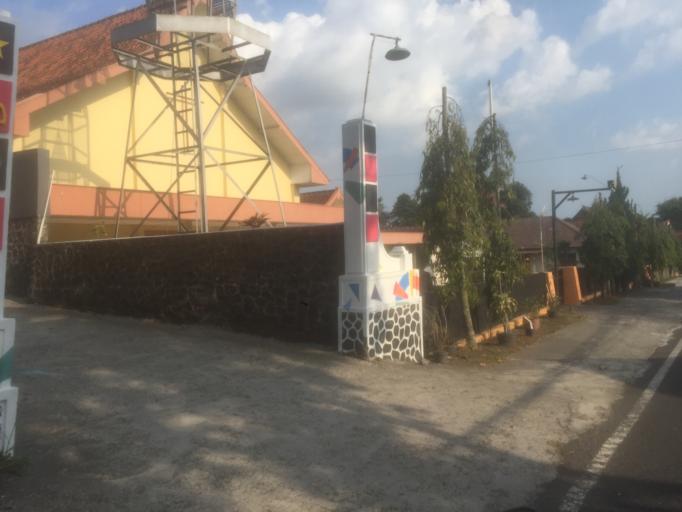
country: ID
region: Daerah Istimewa Yogyakarta
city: Sleman
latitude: -7.6533
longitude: 110.4232
